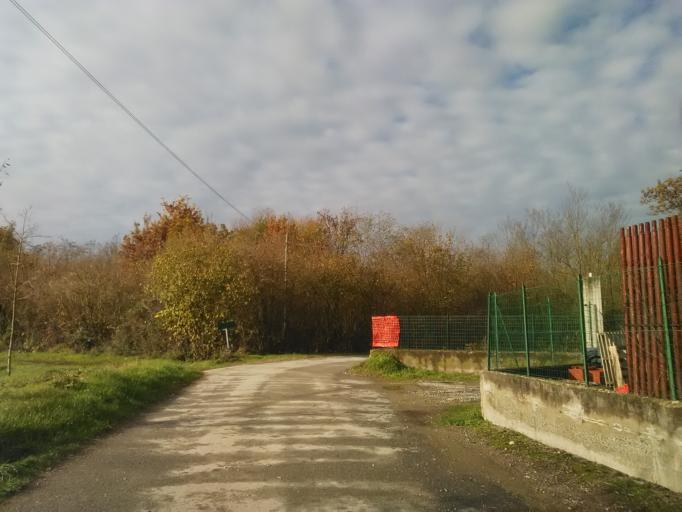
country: IT
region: Piedmont
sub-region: Provincia di Vercelli
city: Alice Castello
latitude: 45.3706
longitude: 8.0609
